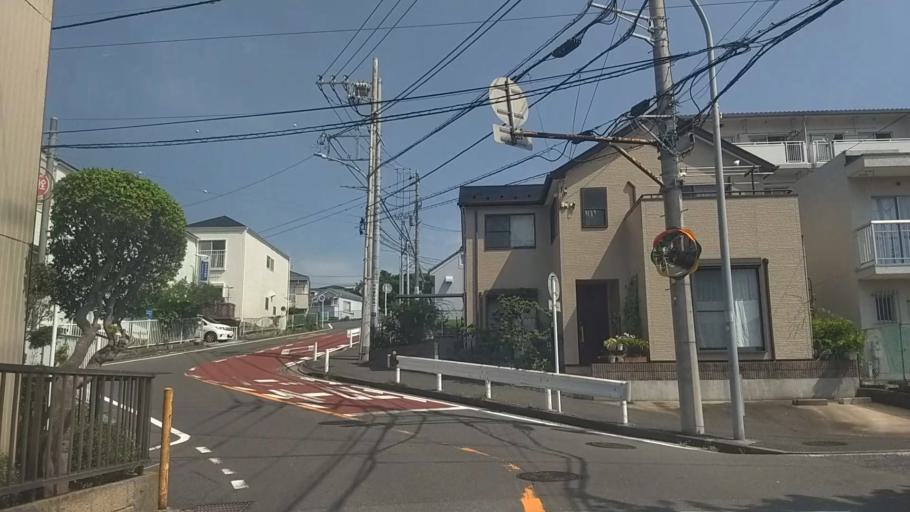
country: JP
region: Kanagawa
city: Zushi
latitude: 35.3297
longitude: 139.6037
